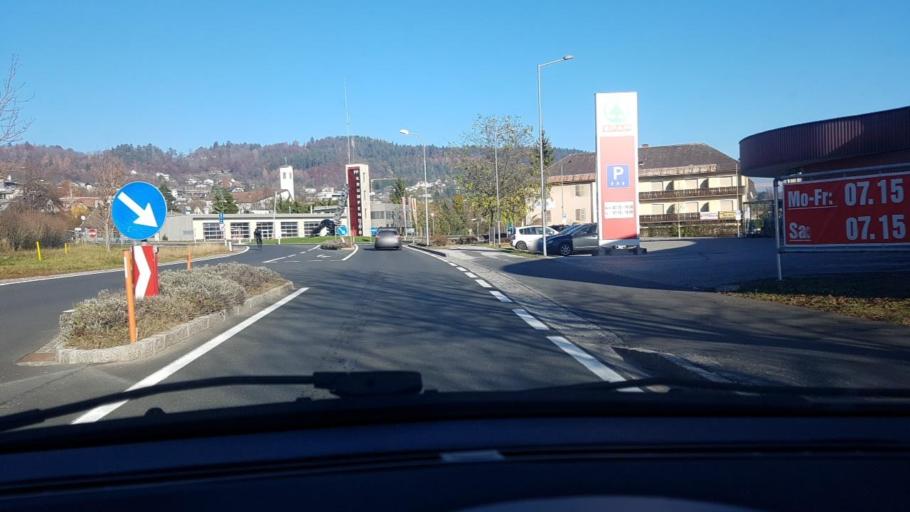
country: AT
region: Carinthia
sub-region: Politischer Bezirk Klagenfurt Land
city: Keutschach am See
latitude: 46.6252
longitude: 14.2036
